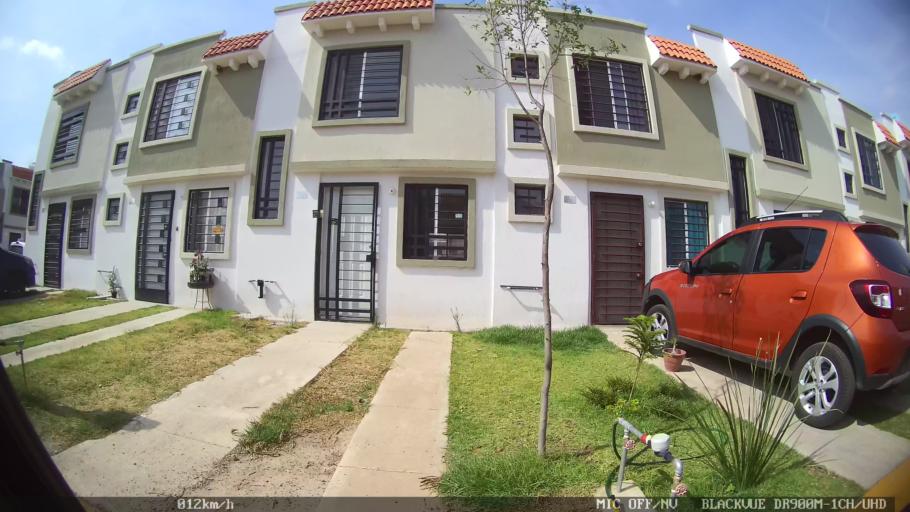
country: MX
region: Jalisco
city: Tonala
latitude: 20.6454
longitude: -103.2298
